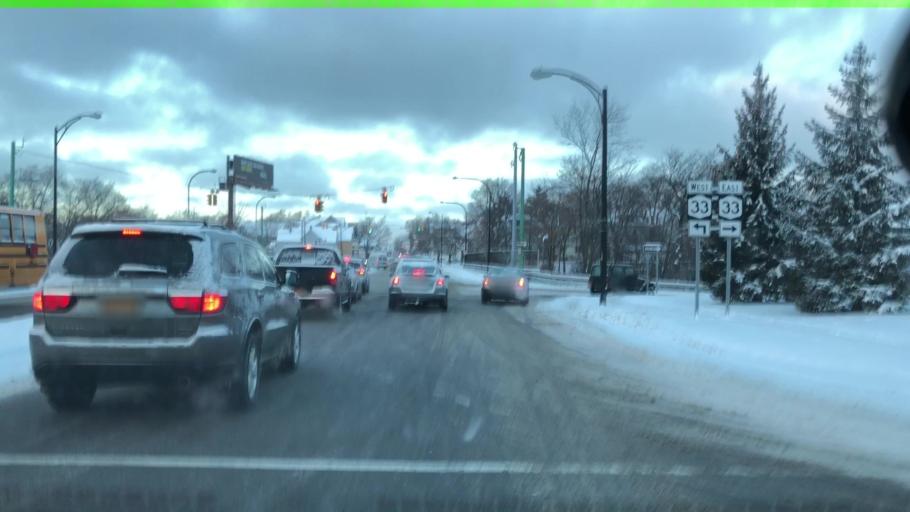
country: US
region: New York
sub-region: Erie County
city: Buffalo
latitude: 42.9038
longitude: -78.8447
